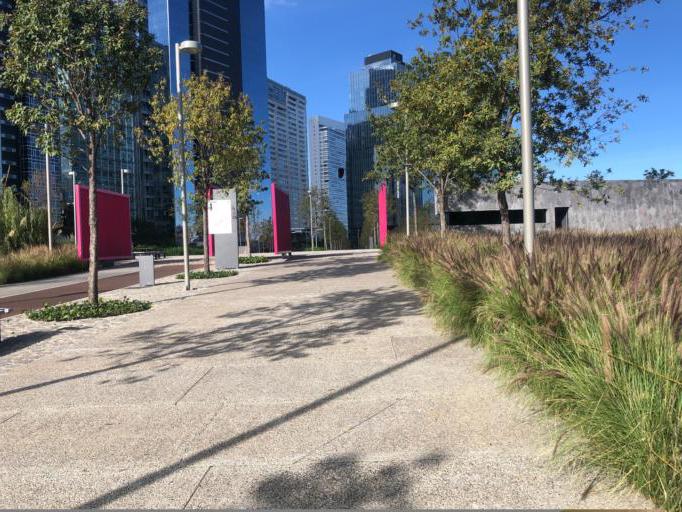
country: MX
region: Mexico City
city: Col. Bosques de las Lomas
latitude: 19.3589
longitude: -99.2683
